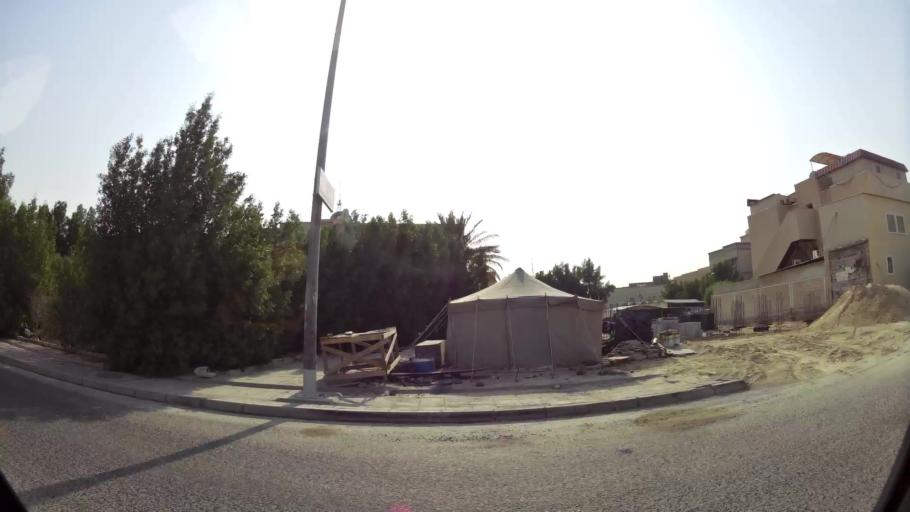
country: KW
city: Al Funaytis
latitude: 29.2194
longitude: 48.0820
